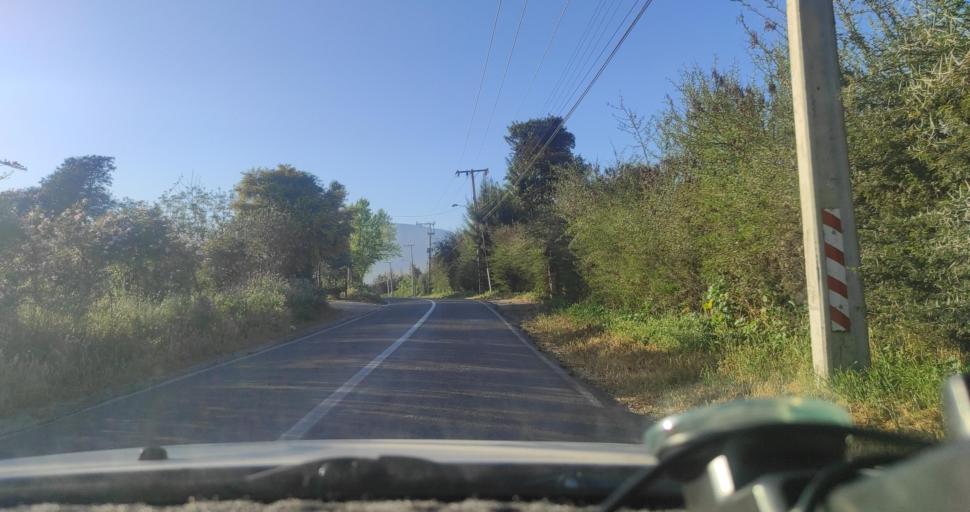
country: CL
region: Valparaiso
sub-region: Provincia de Marga Marga
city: Limache
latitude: -33.0028
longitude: -71.2319
